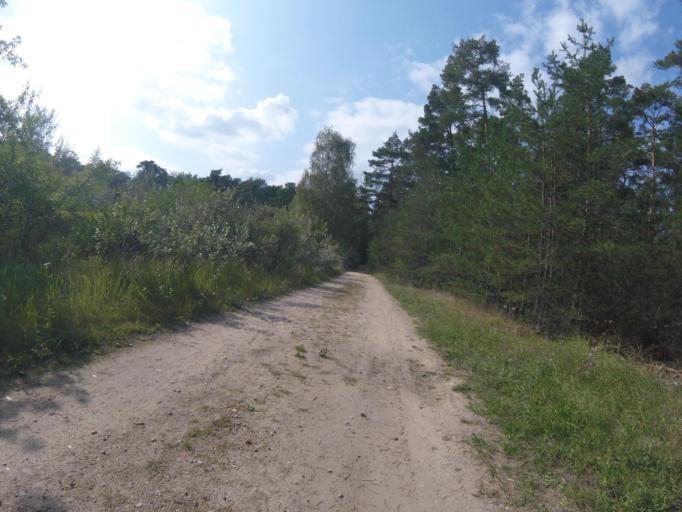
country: DE
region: Brandenburg
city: Bestensee
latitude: 52.2264
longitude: 13.7259
